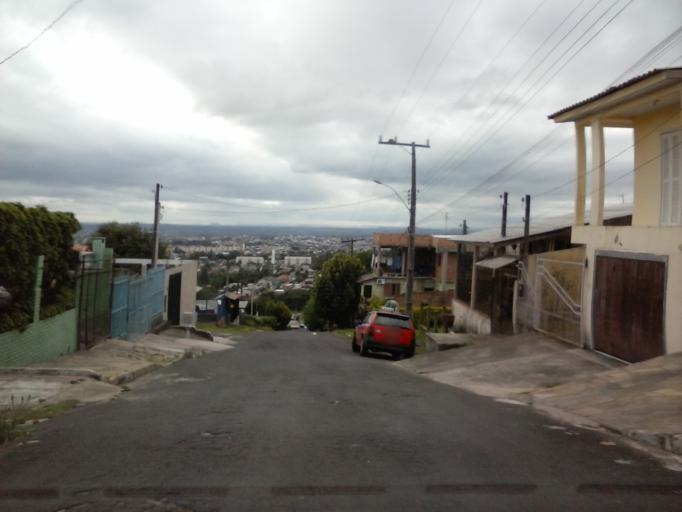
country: BR
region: Rio Grande do Sul
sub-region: Sapucaia Do Sul
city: Sapucaia
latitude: -29.8454
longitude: -51.1100
